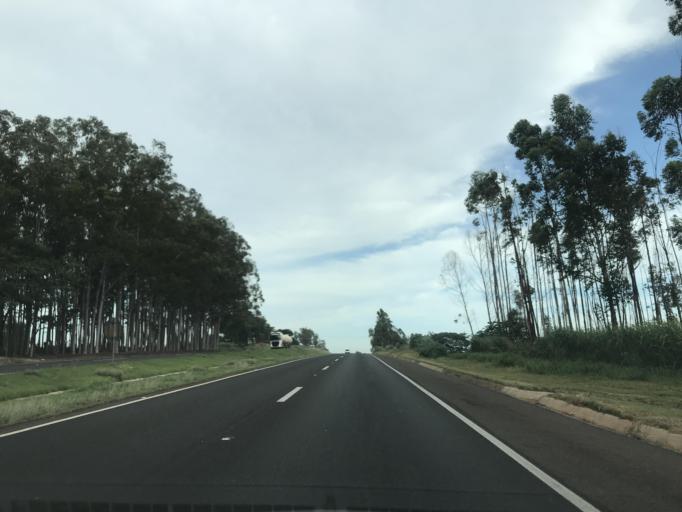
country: BR
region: Parana
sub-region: Alto Parana
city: Alto Parana
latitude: -23.1532
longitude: -52.2695
